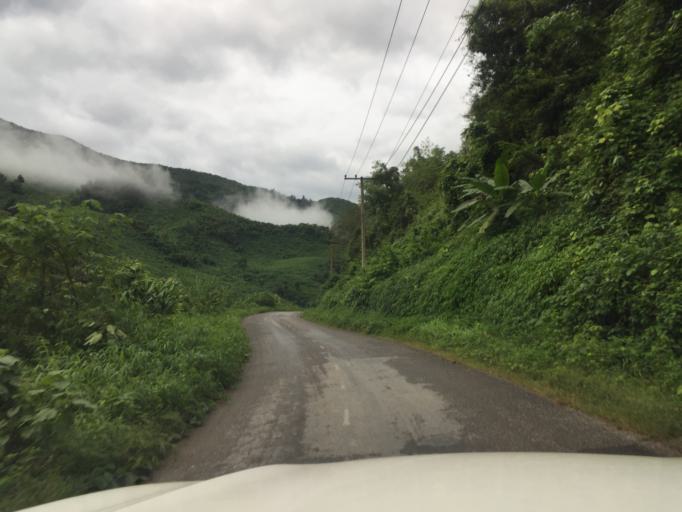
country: LA
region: Oudomxai
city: Muang La
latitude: 21.0328
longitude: 102.2365
